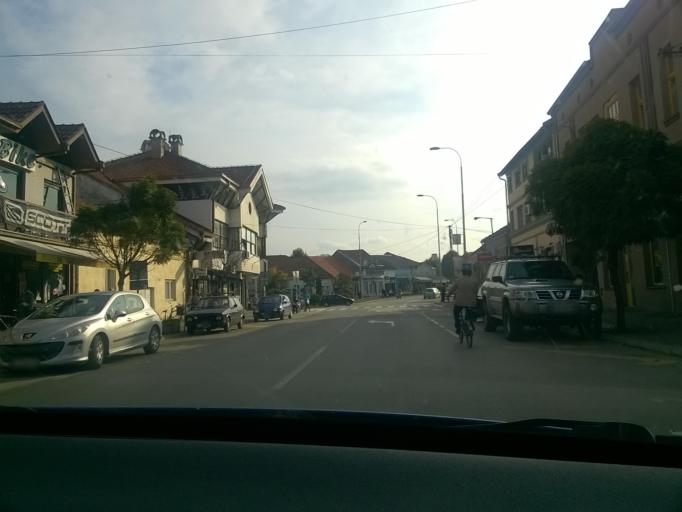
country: RS
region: Central Serbia
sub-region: Pirotski Okrug
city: Pirot
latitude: 43.1604
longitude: 22.5891
